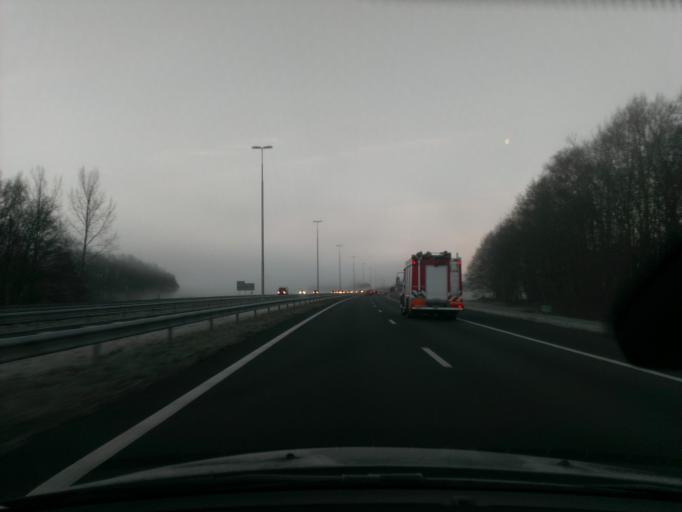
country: NL
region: Gelderland
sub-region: Gemeente Epe
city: Oene
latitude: 52.3574
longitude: 6.0241
